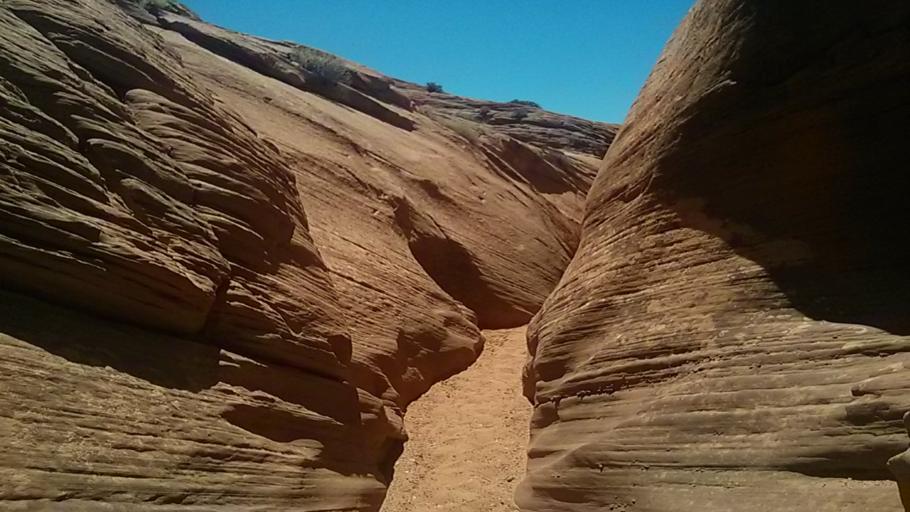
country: US
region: Arizona
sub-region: Coconino County
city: Page
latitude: 37.4850
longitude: -111.2093
